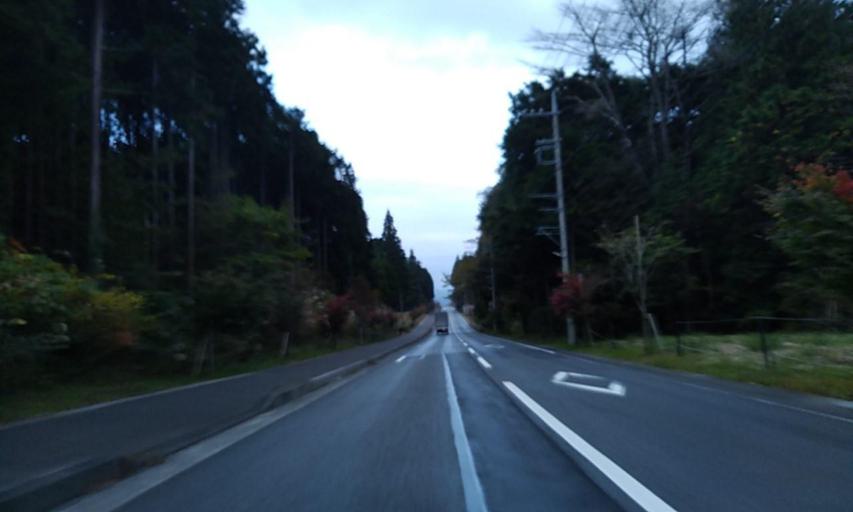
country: JP
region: Shizuoka
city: Gotemba
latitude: 35.3265
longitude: 138.8806
